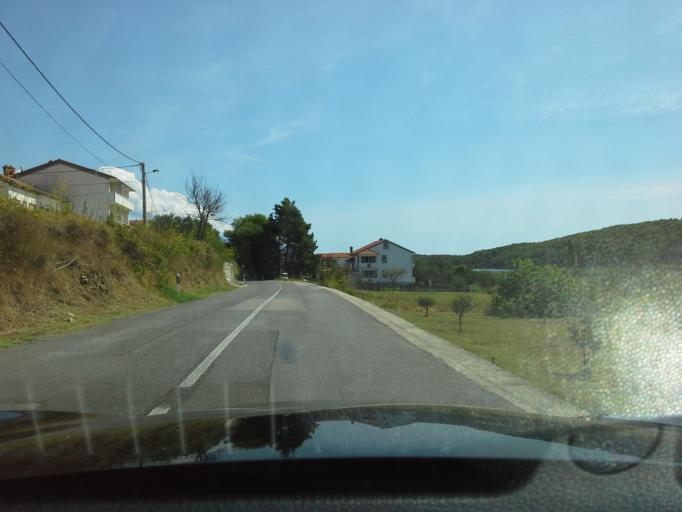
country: HR
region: Primorsko-Goranska
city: Kampor
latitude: 44.7735
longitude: 14.7299
